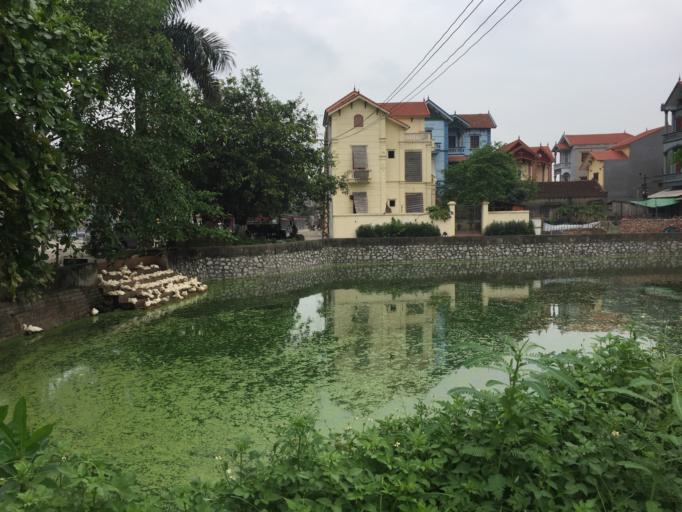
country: VN
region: Bac Ninh
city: Cho
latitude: 21.1144
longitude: 105.9317
